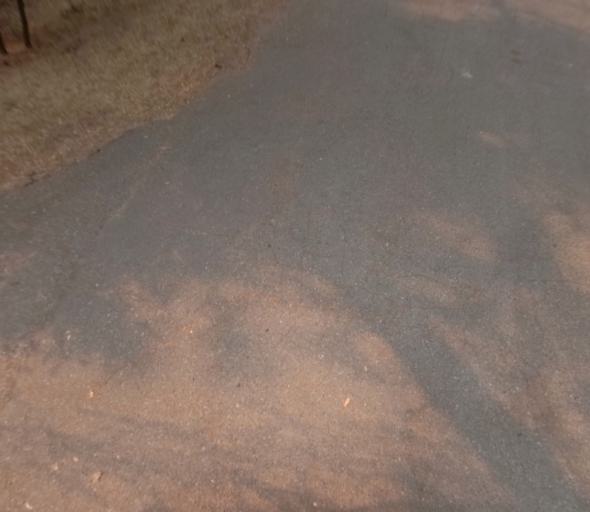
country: US
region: California
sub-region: Madera County
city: Oakhurst
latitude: 37.3060
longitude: -119.6077
